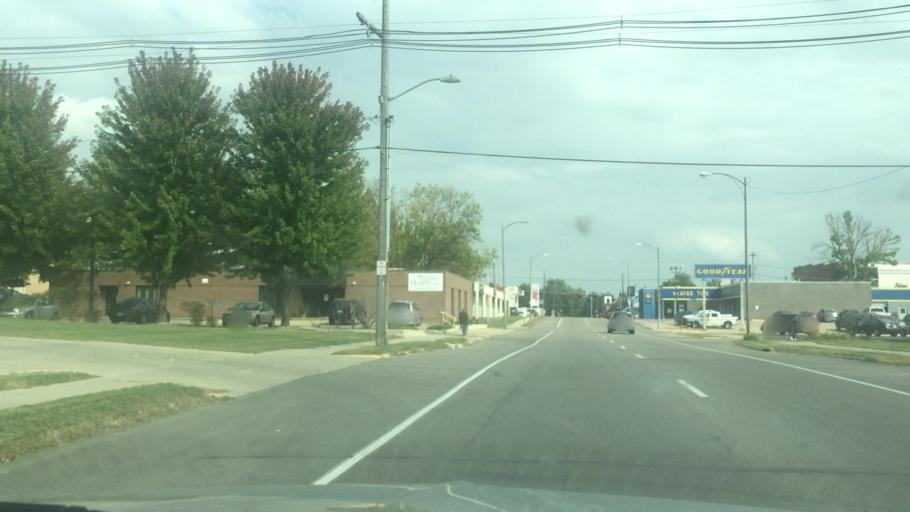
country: US
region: Iowa
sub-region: Marshall County
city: Marshalltown
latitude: 42.0467
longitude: -92.9107
